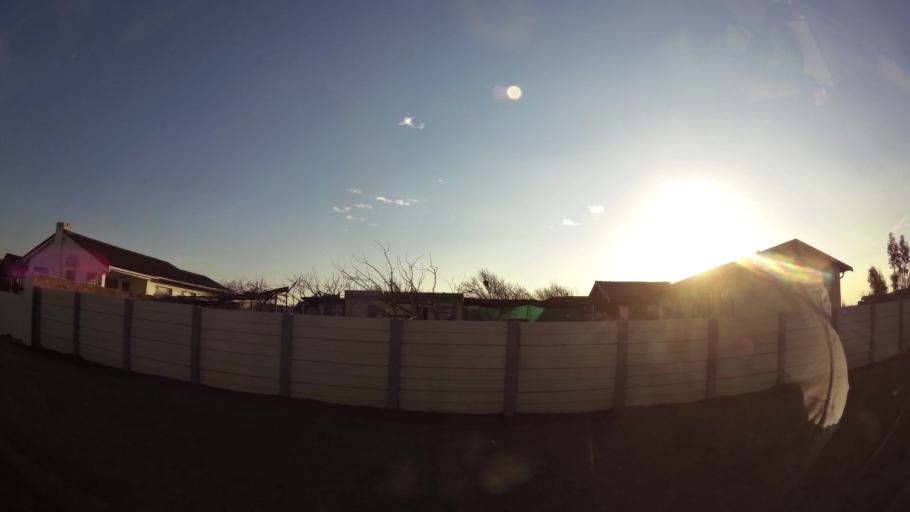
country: ZA
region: Gauteng
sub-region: West Rand District Municipality
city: Randfontein
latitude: -26.2025
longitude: 27.6520
